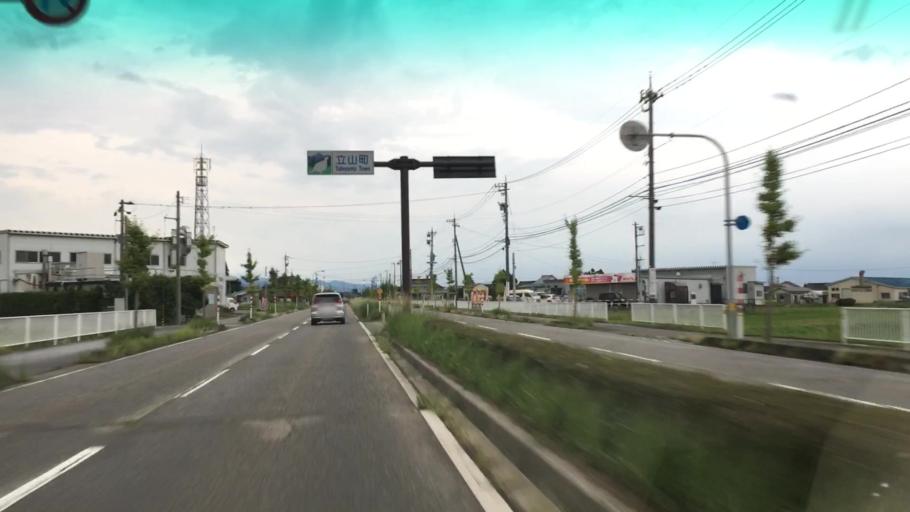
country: JP
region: Toyama
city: Kamiichi
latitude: 36.6921
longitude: 137.3423
